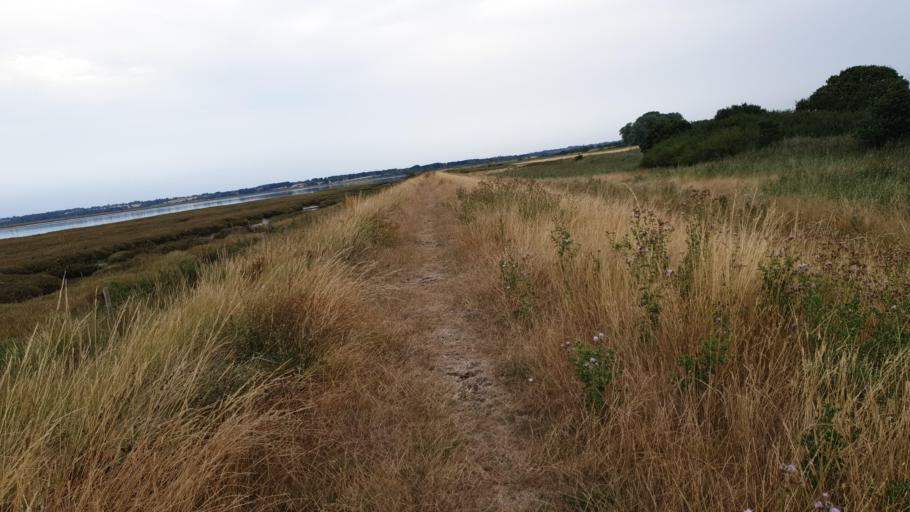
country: GB
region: England
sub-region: Essex
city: Brightlingsea
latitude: 51.8167
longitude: 0.9958
